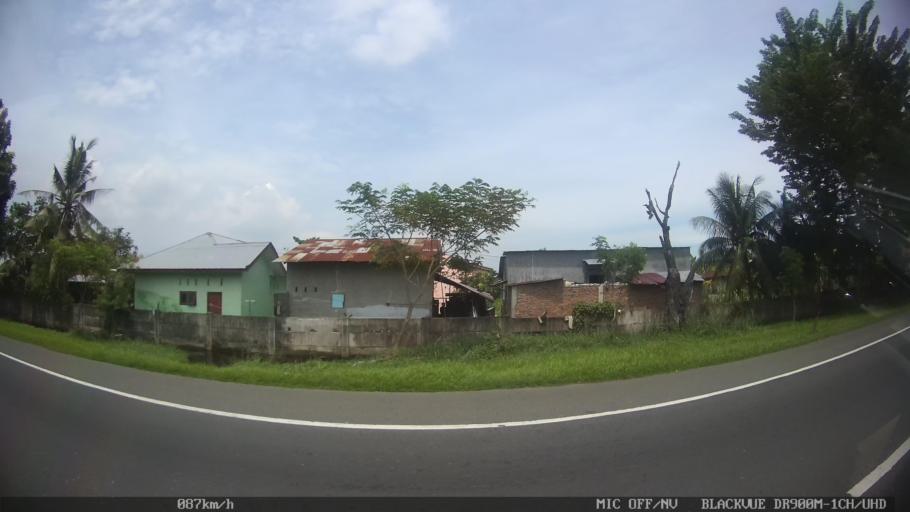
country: ID
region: North Sumatra
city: Labuhan Deli
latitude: 3.7165
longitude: 98.6825
